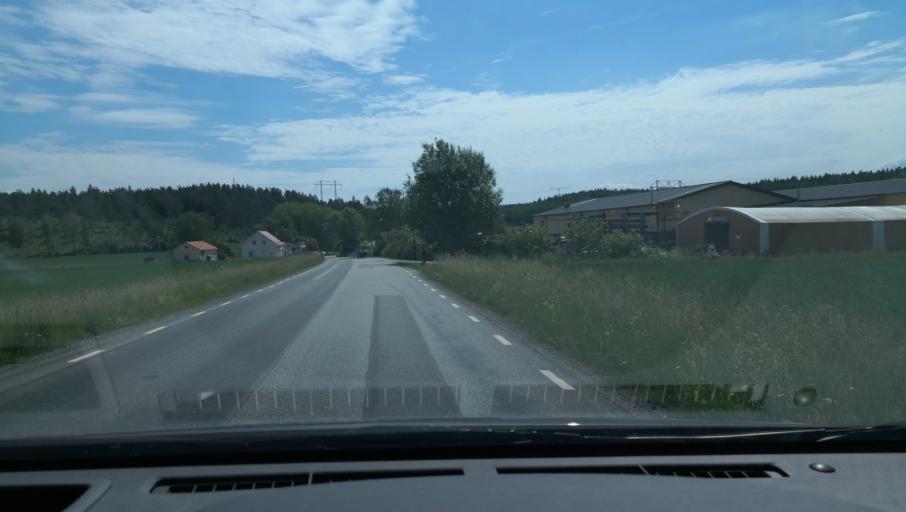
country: SE
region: Uppsala
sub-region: Habo Kommun
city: Balsta
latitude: 59.6644
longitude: 17.4482
